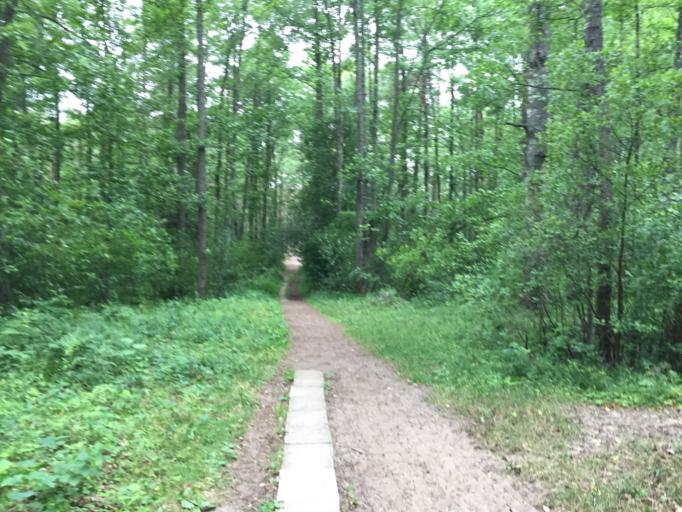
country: LV
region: Carnikava
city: Carnikava
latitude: 57.1195
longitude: 24.2218
